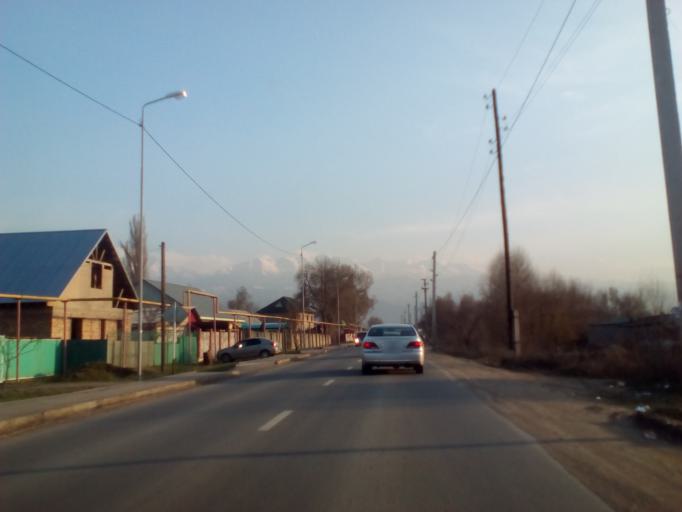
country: KZ
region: Almaty Oblysy
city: Burunday
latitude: 43.2444
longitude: 76.7464
